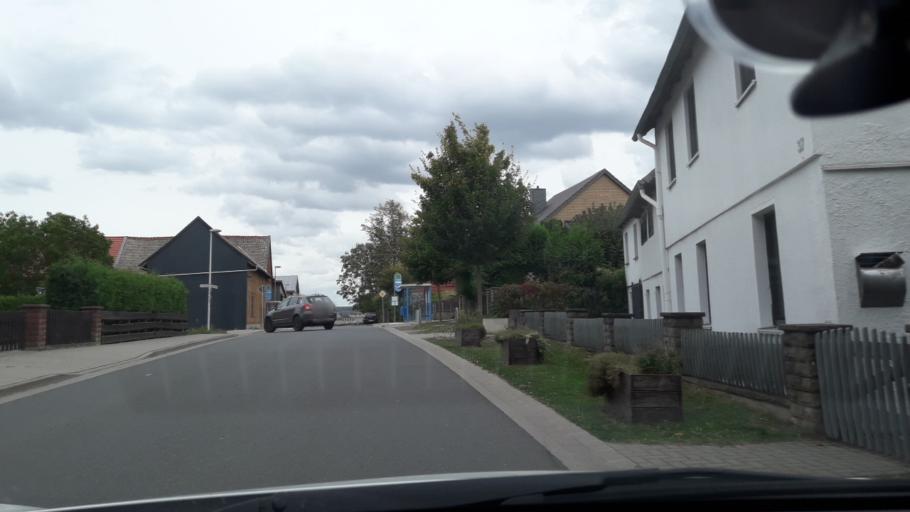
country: DE
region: Lower Saxony
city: Cramme
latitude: 52.0971
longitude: 10.4290
